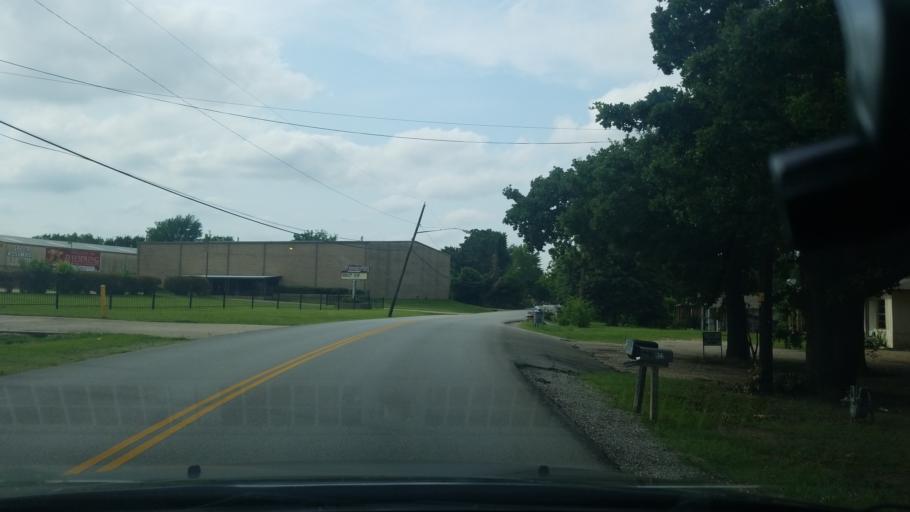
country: US
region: Texas
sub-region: Dallas County
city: Balch Springs
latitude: 32.7593
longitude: -96.6432
